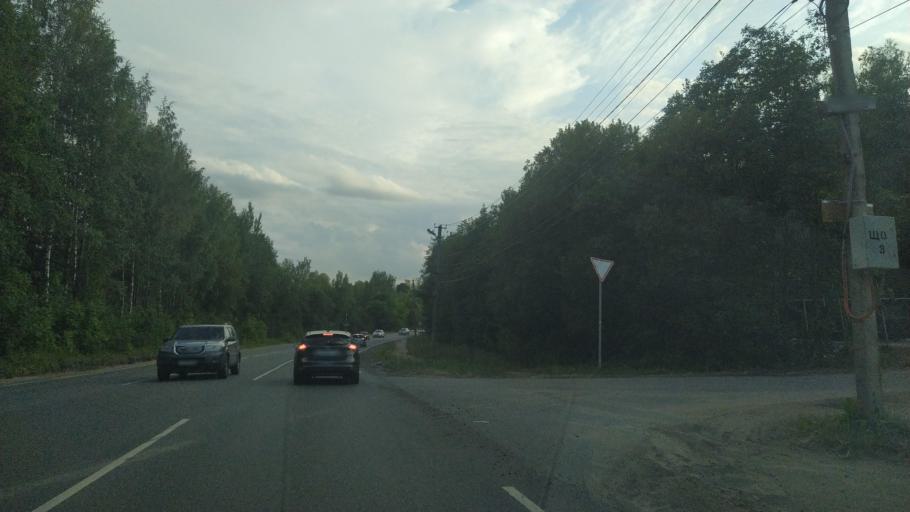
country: RU
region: Leningrad
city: Toksovo
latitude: 60.1565
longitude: 30.5312
